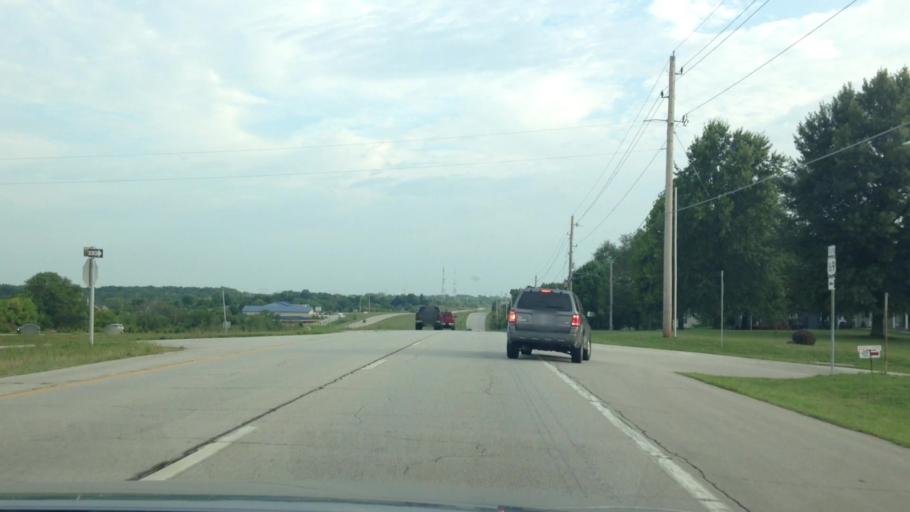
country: US
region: Missouri
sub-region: Clay County
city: Smithville
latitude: 39.3547
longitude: -94.5841
